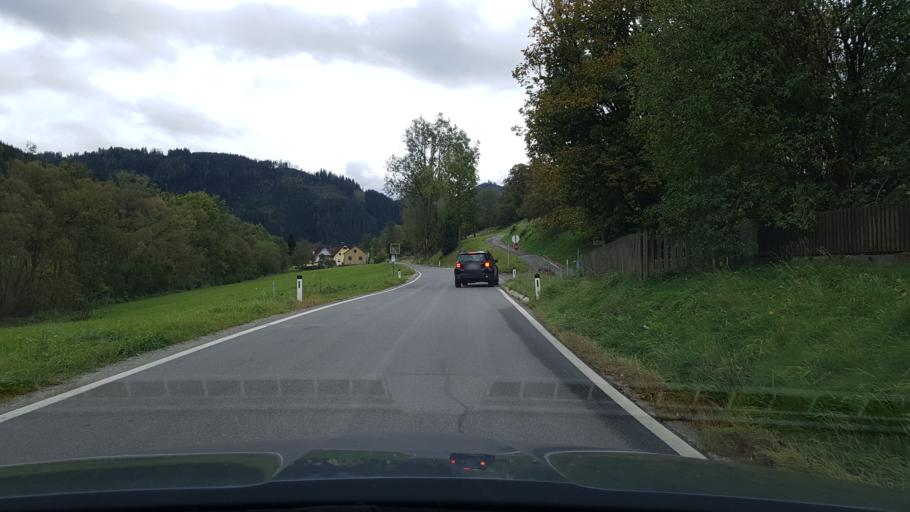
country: AT
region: Styria
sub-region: Politischer Bezirk Bruck-Muerzzuschlag
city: Allerheiligen im Muerztal
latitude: 47.4734
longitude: 15.4155
